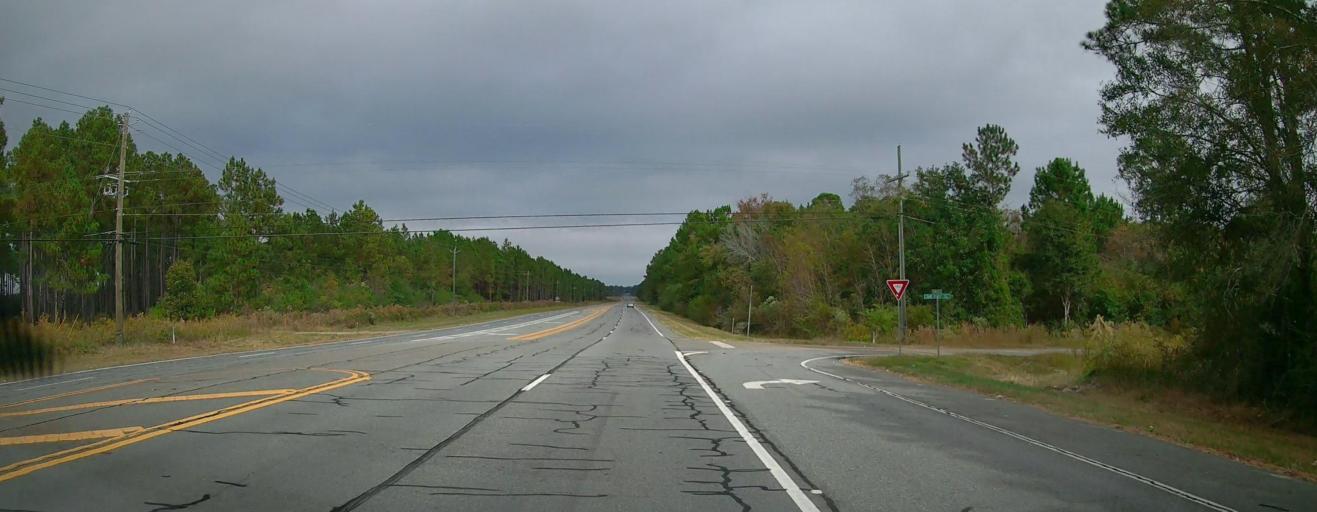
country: US
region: Georgia
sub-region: Colquitt County
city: Moultrie
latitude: 31.2305
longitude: -83.7440
